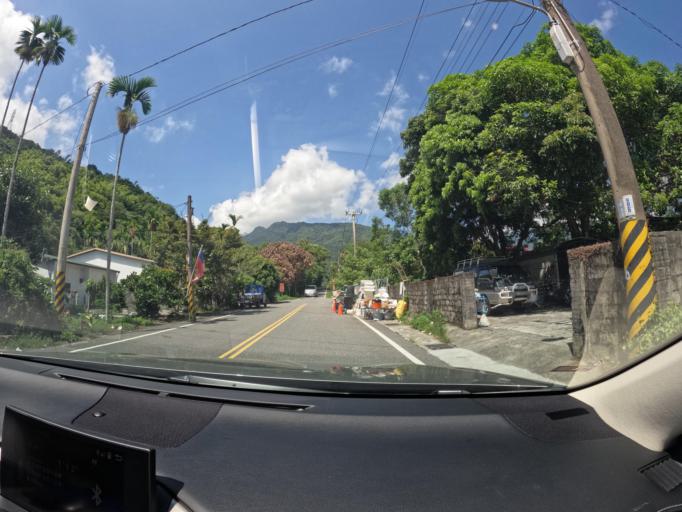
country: TW
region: Taiwan
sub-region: Hualien
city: Hualian
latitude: 23.6858
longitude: 121.4082
